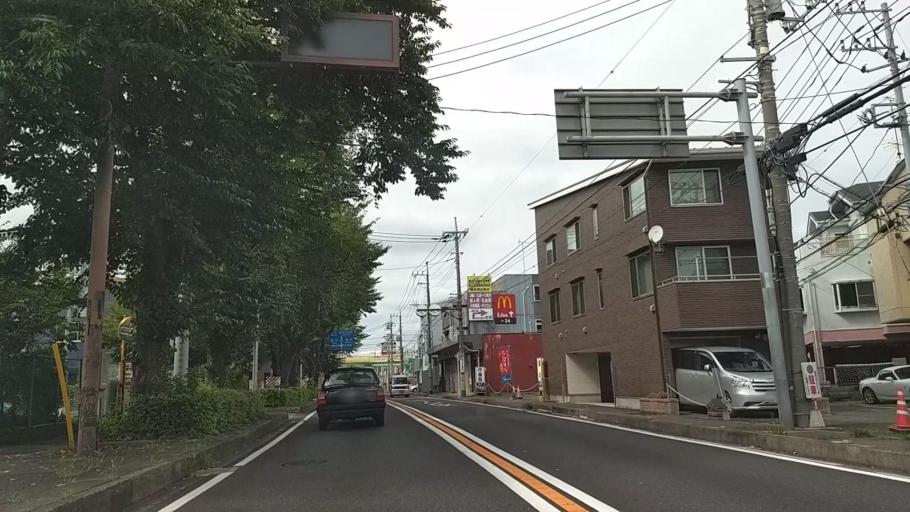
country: JP
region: Kanagawa
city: Minami-rinkan
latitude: 35.4618
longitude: 139.4675
